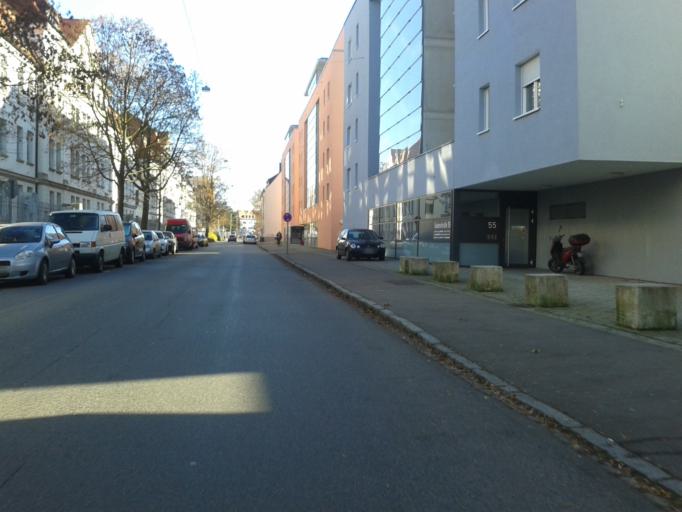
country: DE
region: Baden-Wuerttemberg
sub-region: Tuebingen Region
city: Ulm
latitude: 48.3910
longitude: 9.9702
